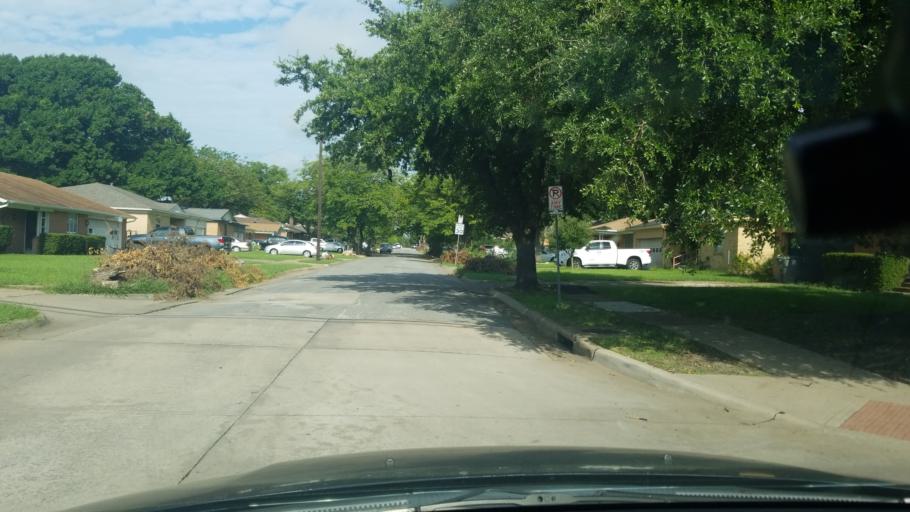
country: US
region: Texas
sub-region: Dallas County
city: Balch Springs
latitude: 32.7478
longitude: -96.6656
